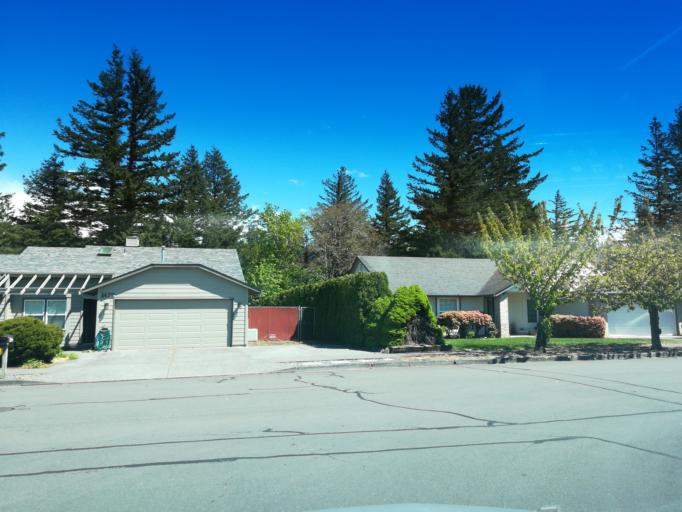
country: US
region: Oregon
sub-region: Multnomah County
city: Troutdale
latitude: 45.5307
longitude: -122.3764
